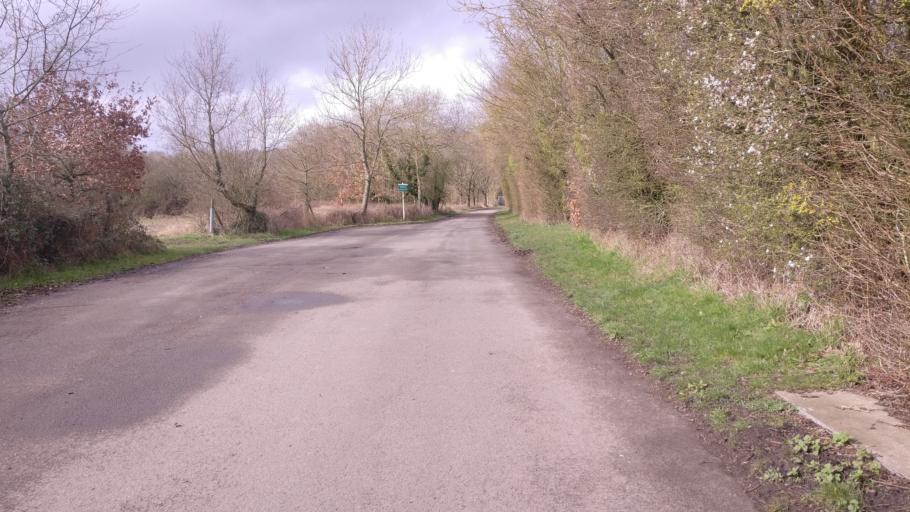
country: GB
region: England
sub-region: West Berkshire
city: Stratfield Mortimer
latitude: 51.3328
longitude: -1.0717
